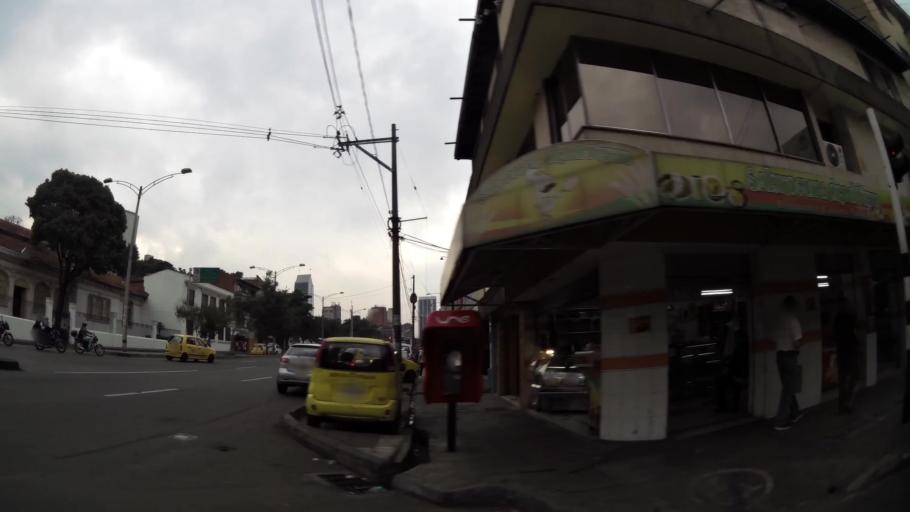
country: CO
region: Antioquia
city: Medellin
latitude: 6.2579
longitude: -75.5666
